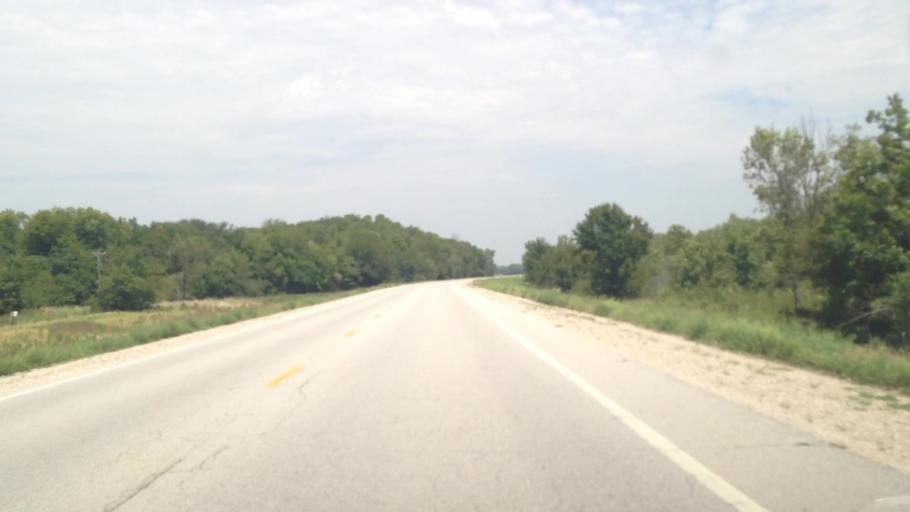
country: US
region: Kansas
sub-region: Neosho County
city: Erie
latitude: 37.5380
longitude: -95.2700
